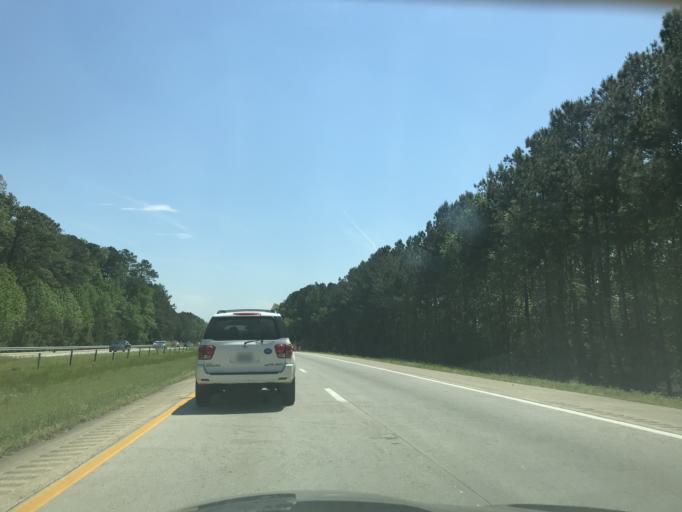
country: US
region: North Carolina
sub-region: Wake County
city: Garner
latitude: 35.5796
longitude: -78.5766
